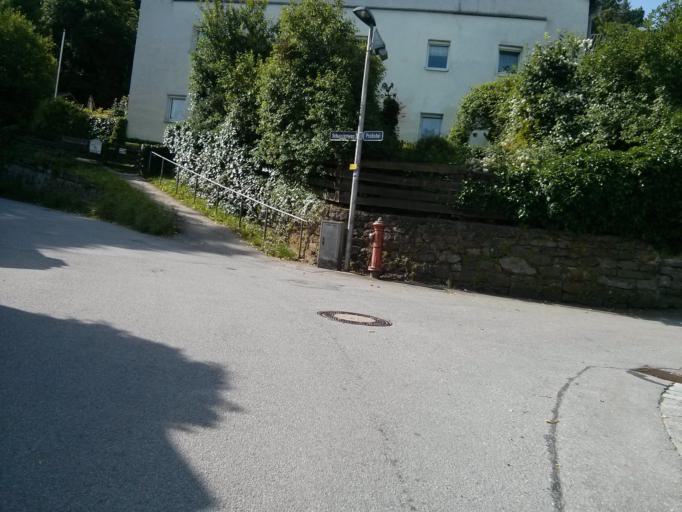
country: DE
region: Bavaria
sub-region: Lower Bavaria
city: Deggendorf
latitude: 48.8290
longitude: 12.9646
